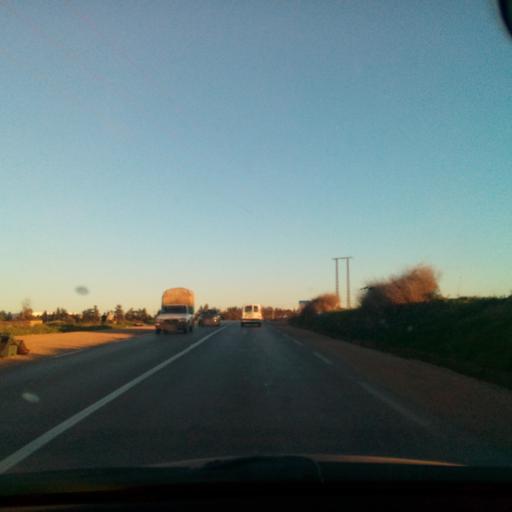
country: DZ
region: Relizane
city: Relizane
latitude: 35.7349
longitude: 0.2977
